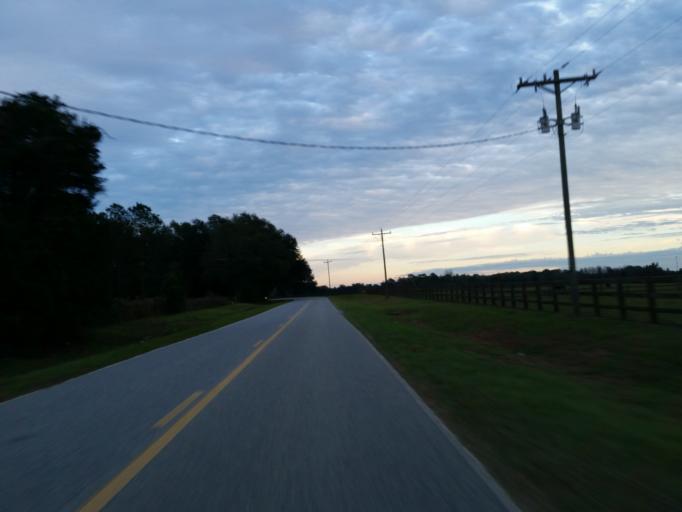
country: US
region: Florida
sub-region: Hamilton County
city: Jasper
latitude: 30.5230
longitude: -83.0813
